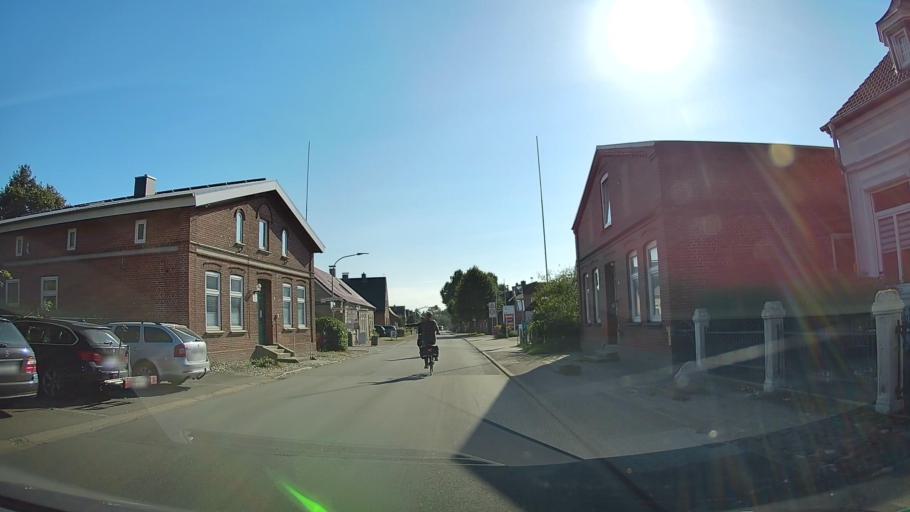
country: DE
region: Schleswig-Holstein
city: Fehmarn
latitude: 54.4500
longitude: 11.1452
